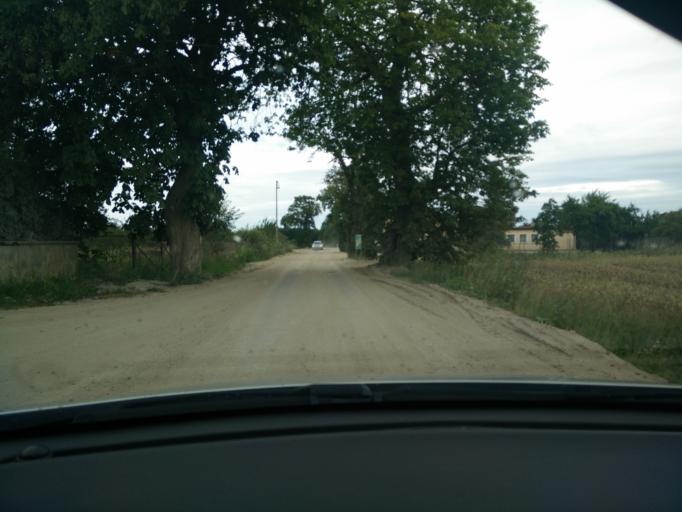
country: PL
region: Pomeranian Voivodeship
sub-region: Powiat pucki
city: Mrzezino
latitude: 54.6543
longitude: 18.4343
